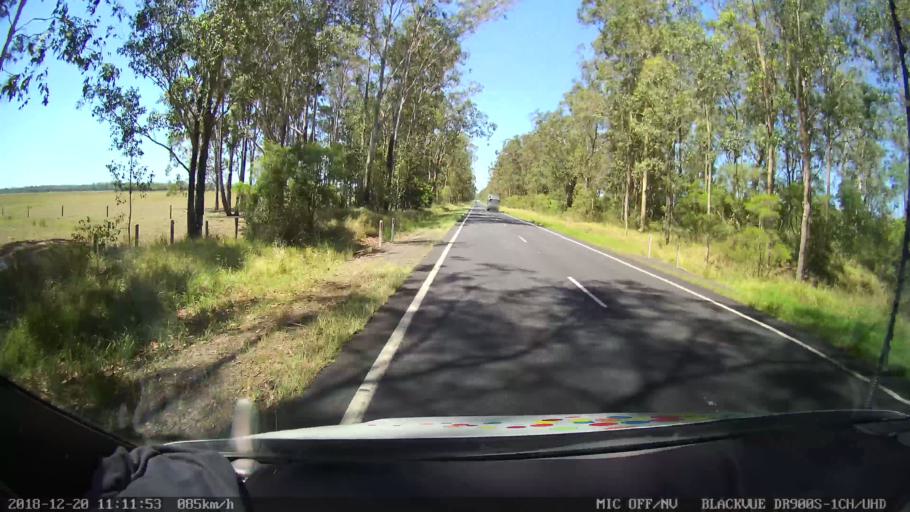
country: AU
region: New South Wales
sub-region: Richmond Valley
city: Casino
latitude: -28.9667
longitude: 153.0125
